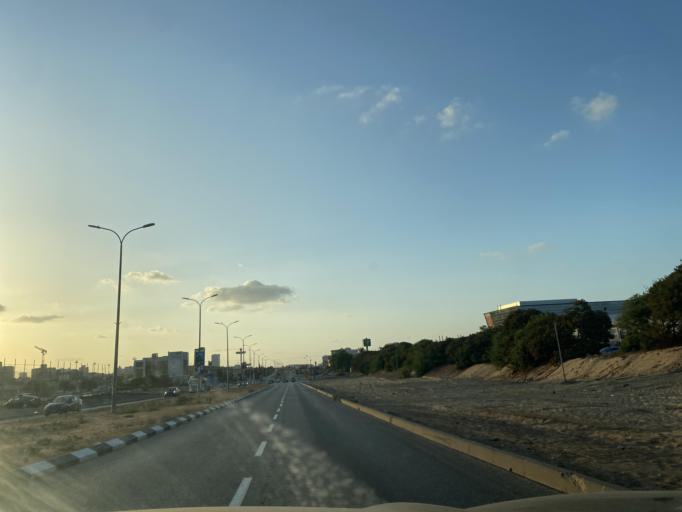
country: IL
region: Southern District
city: Ashdod
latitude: 31.8084
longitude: 34.6616
